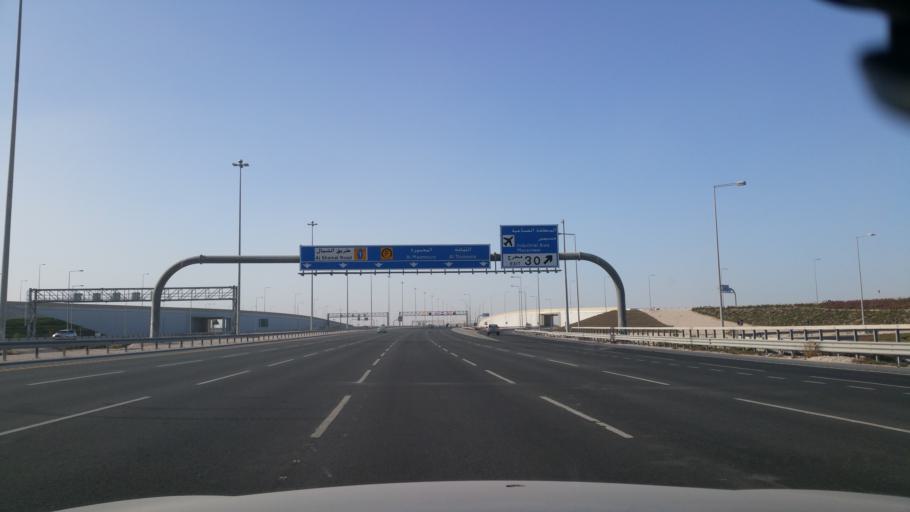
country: QA
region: Al Wakrah
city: Al Wukayr
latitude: 25.1843
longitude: 51.5482
